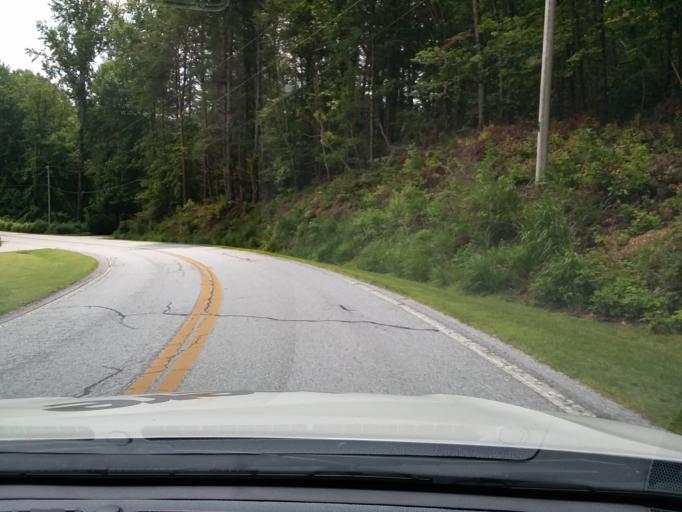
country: US
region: Georgia
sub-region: Rabun County
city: Mountain City
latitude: 34.9652
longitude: -83.1865
